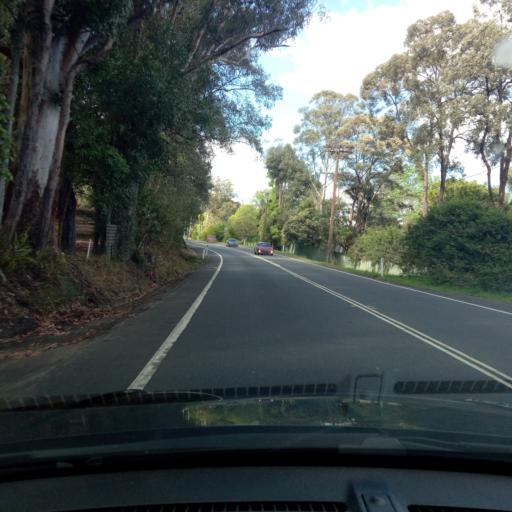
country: AU
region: New South Wales
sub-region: Gosford Shire
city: Lisarow
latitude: -33.3862
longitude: 151.3542
